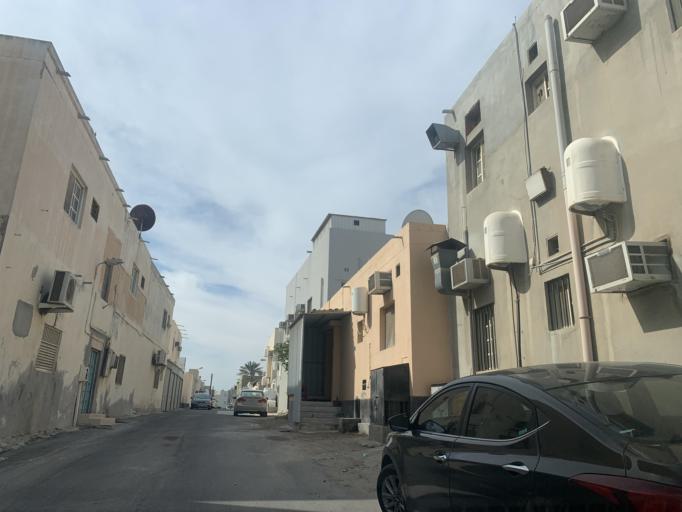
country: BH
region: Central Governorate
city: Madinat Hamad
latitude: 26.1185
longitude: 50.4816
